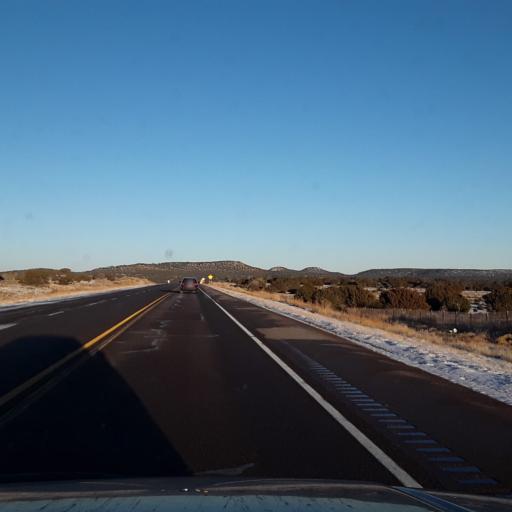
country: US
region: New Mexico
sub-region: Lincoln County
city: Carrizozo
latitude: 34.2359
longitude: -105.6136
